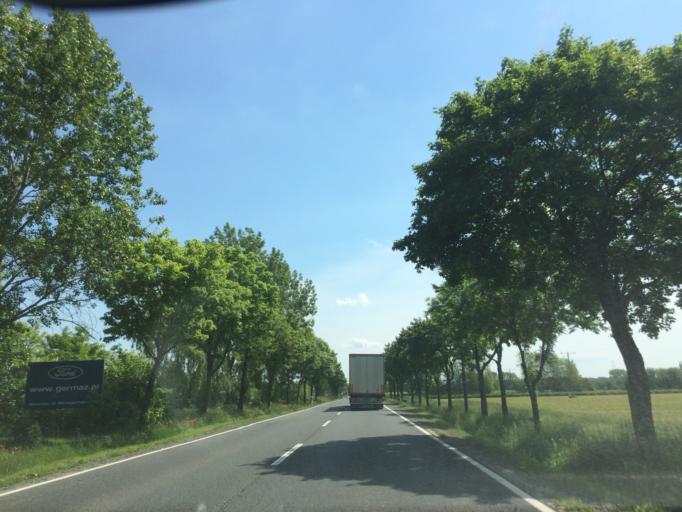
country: PL
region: Lower Silesian Voivodeship
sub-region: Powiat wroclawski
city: Sobotka
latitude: 50.9532
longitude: 16.7687
